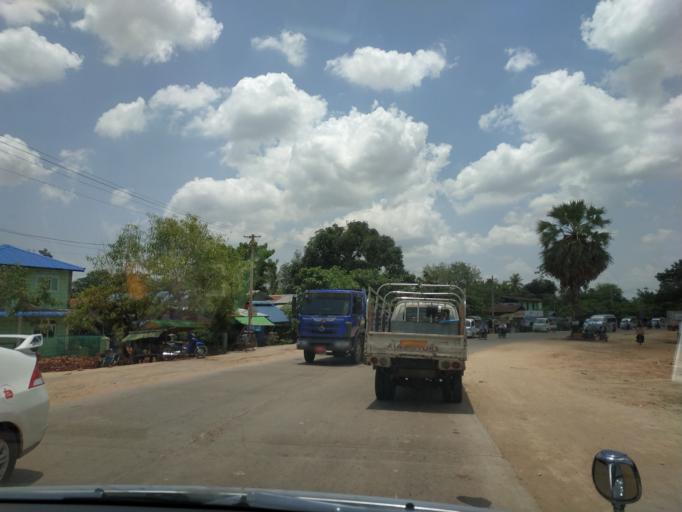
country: MM
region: Bago
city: Bago
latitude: 17.4763
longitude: 96.5195
